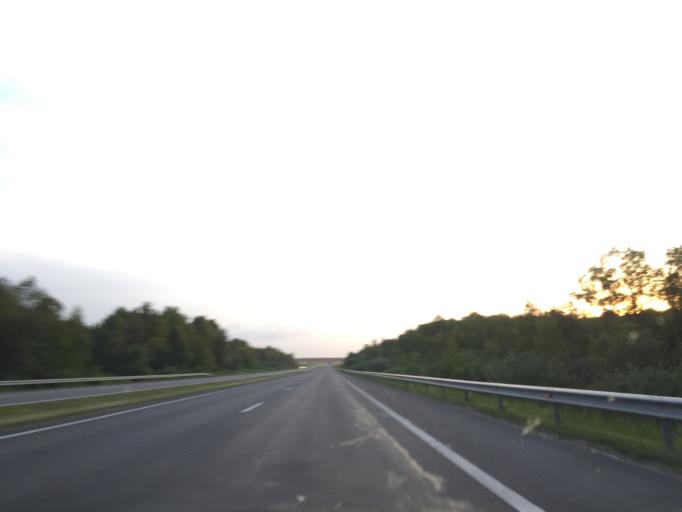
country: LT
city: Kursenai
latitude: 55.9897
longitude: 23.0619
